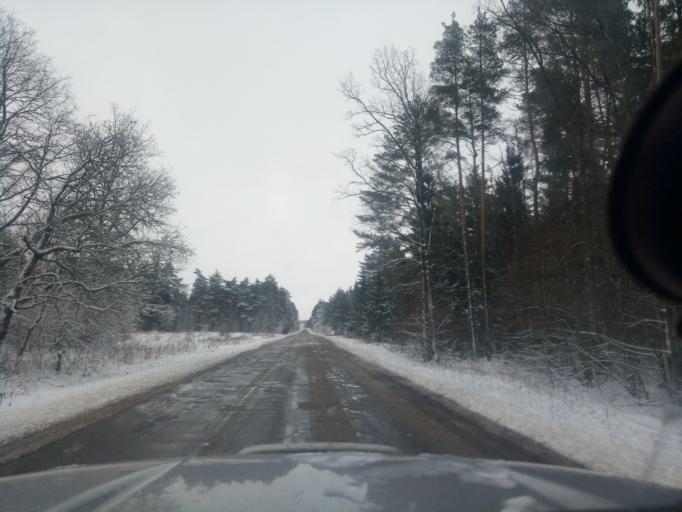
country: BY
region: Minsk
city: Tsimkavichy
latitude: 53.0520
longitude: 26.8855
